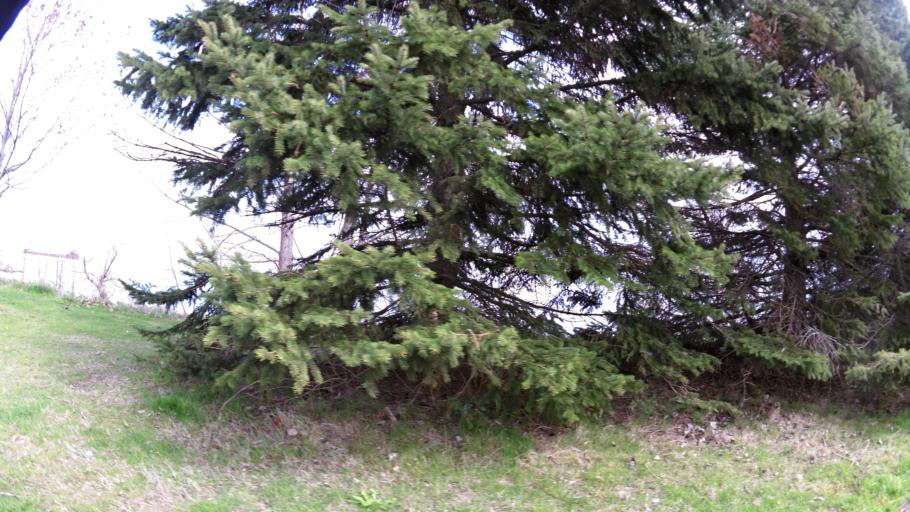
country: CA
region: Ontario
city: Mississauga
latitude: 43.5465
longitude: -79.5823
